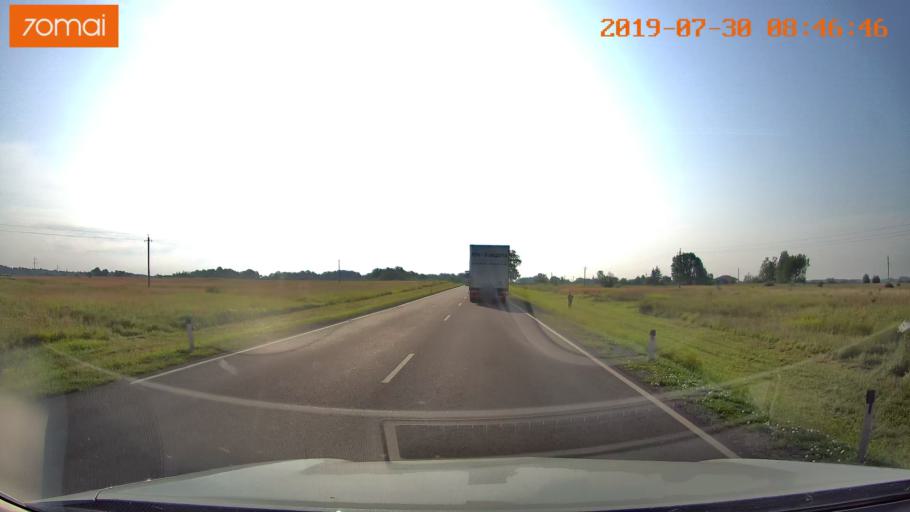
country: RU
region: Kaliningrad
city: Chernyakhovsk
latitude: 54.6218
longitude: 21.8912
